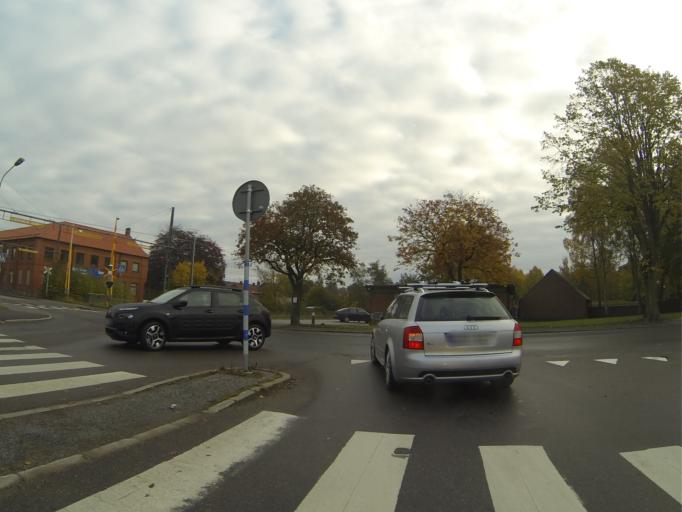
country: SE
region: Skane
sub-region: Tomelilla Kommun
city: Tomelilla
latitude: 55.5419
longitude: 13.9537
